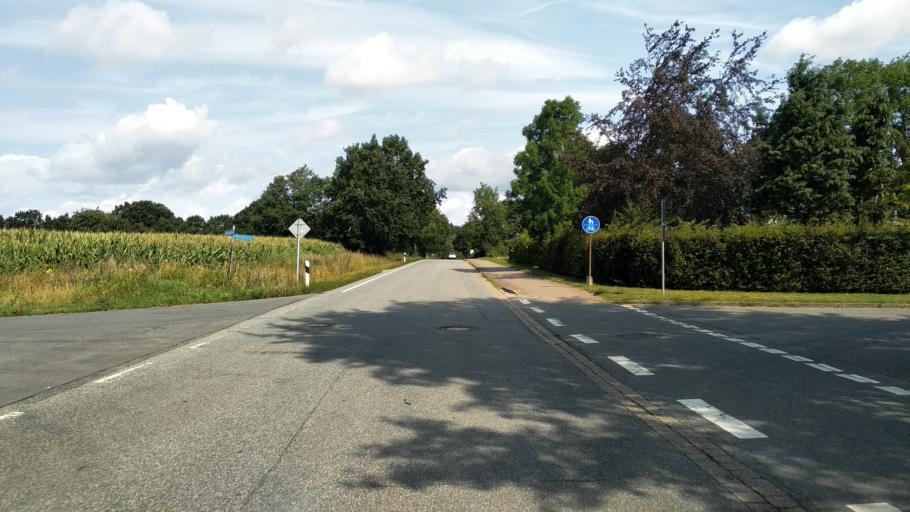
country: DE
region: Schleswig-Holstein
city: Selk
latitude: 54.4723
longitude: 9.5667
